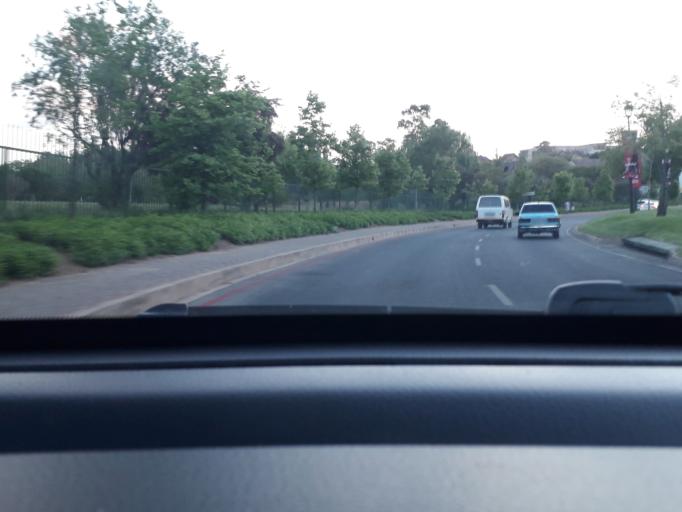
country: ZA
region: Gauteng
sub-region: City of Johannesburg Metropolitan Municipality
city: Diepsloot
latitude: -26.0258
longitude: 28.0162
